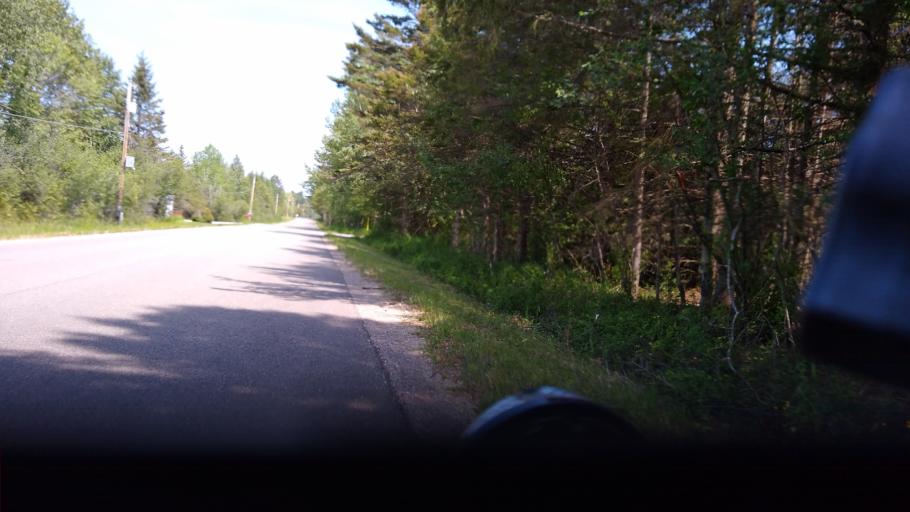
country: US
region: Michigan
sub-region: Delta County
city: Escanaba
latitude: 45.7101
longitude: -87.1268
